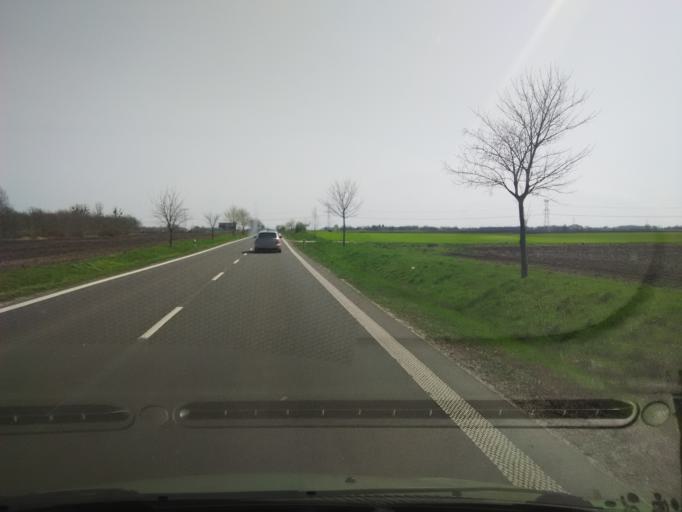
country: SK
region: Nitriansky
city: Surany
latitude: 48.0746
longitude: 18.0861
